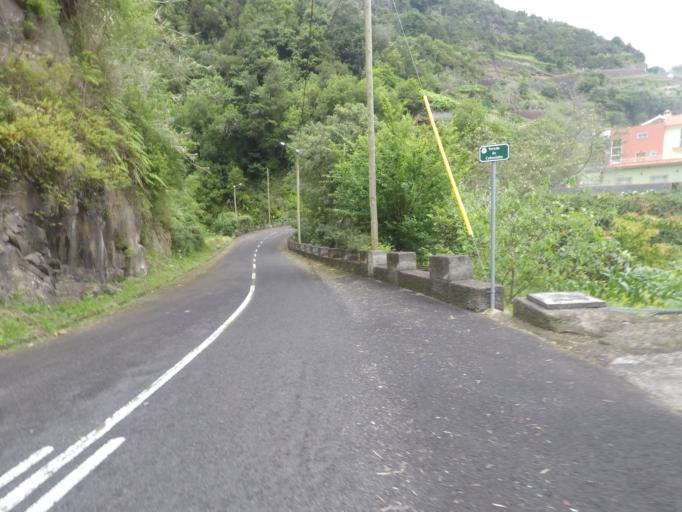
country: PT
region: Madeira
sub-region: Santana
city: Santana
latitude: 32.7654
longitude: -16.8760
